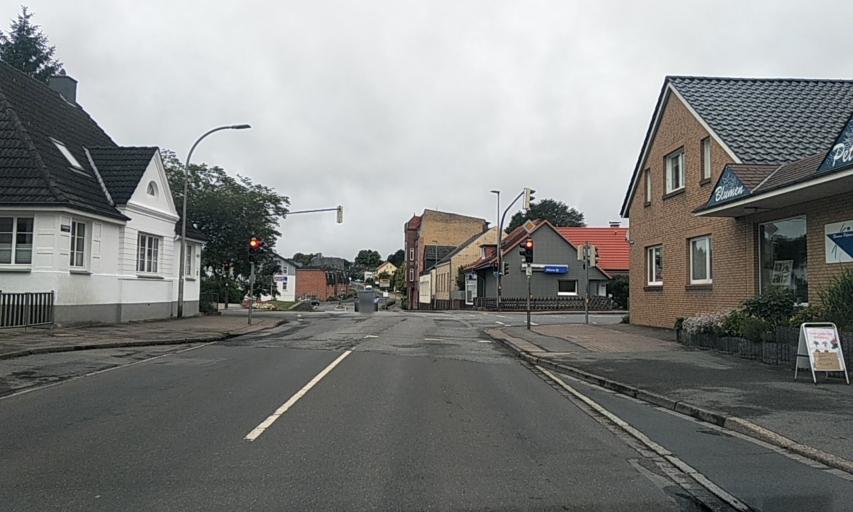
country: DE
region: Schleswig-Holstein
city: Schleswig
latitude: 54.5229
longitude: 9.5463
